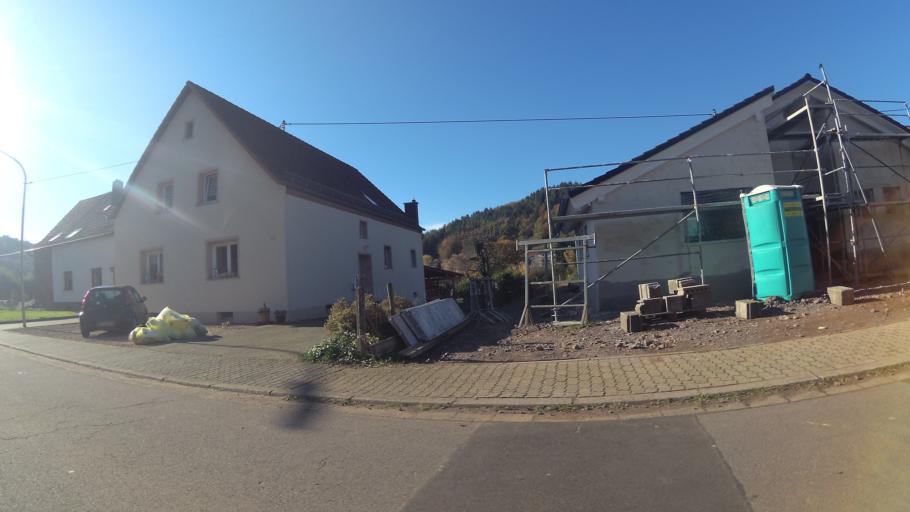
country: DE
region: Saarland
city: Losheim
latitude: 49.4627
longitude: 6.7558
